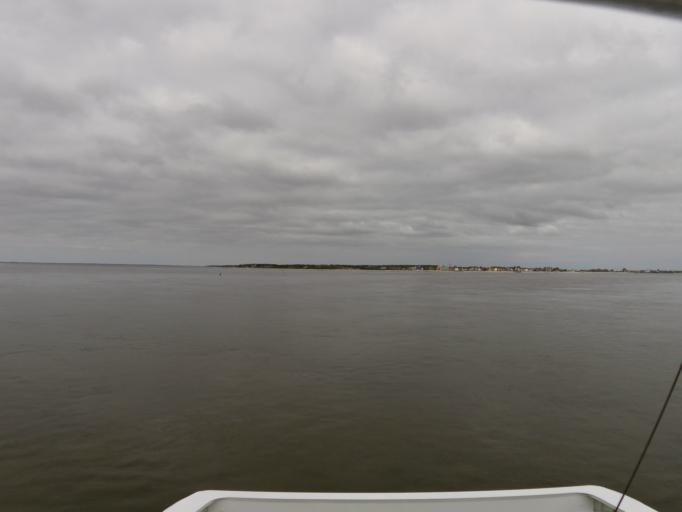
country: DE
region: Schleswig-Holstein
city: Wyk auf Fohr
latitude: 54.6760
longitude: 8.5968
